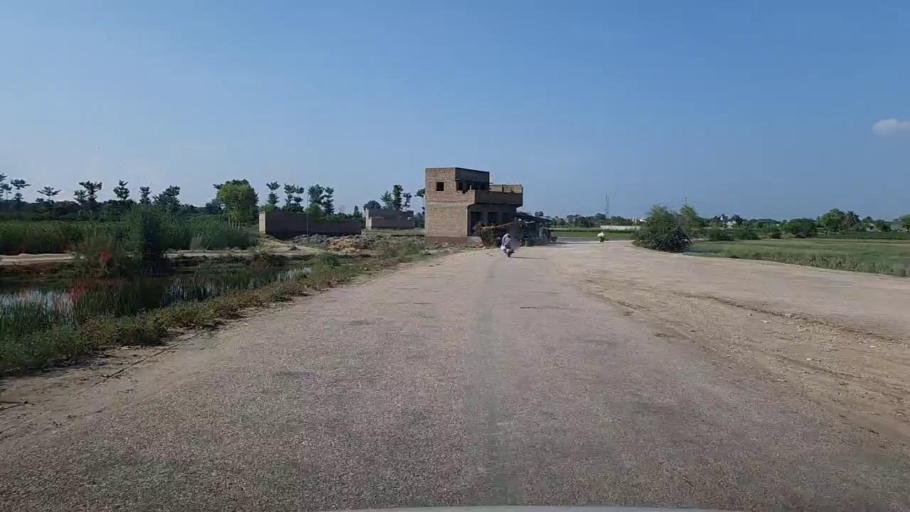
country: PK
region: Sindh
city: Kandiaro
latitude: 27.0749
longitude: 68.3123
